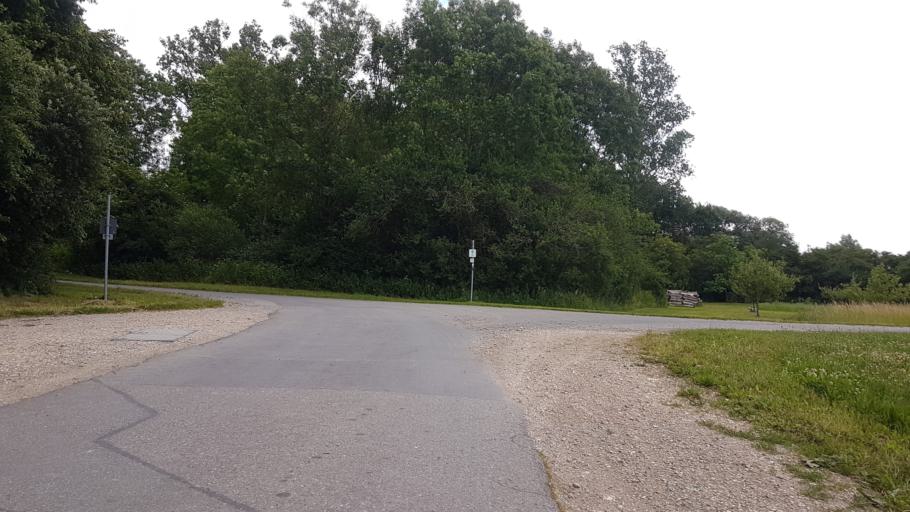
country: DE
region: Baden-Wuerttemberg
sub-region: Tuebingen Region
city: Herbertingen
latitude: 48.0703
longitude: 9.3960
